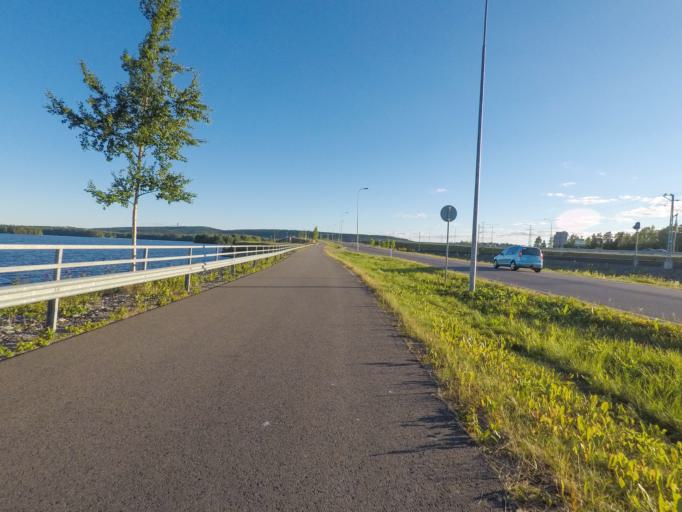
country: FI
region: Northern Savo
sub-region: Kuopio
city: Kuopio
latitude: 62.9515
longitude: 27.6798
